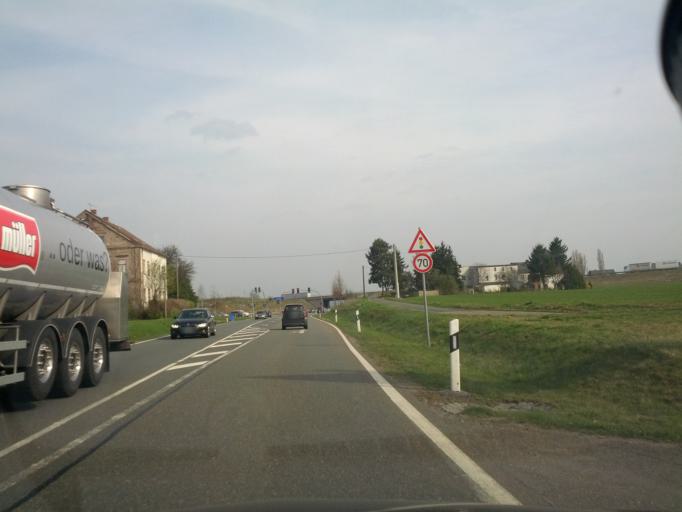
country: DE
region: Saxony
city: Reinsdorf
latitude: 50.6827
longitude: 12.5785
